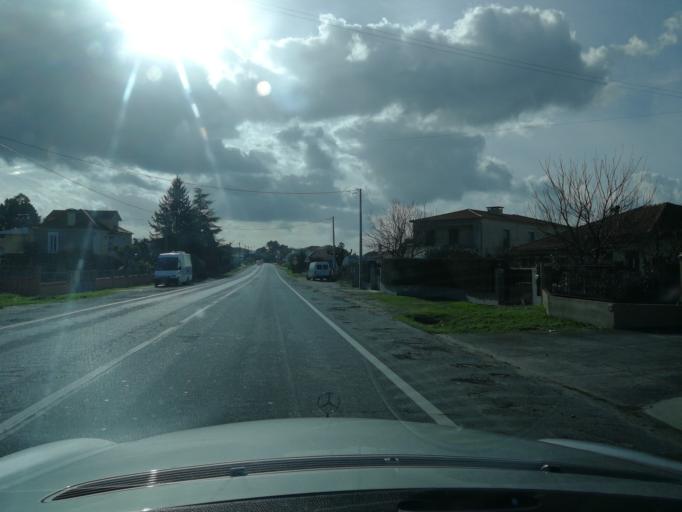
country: PT
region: Viana do Castelo
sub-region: Valenca
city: Valenza
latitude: 42.0306
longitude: -8.6308
